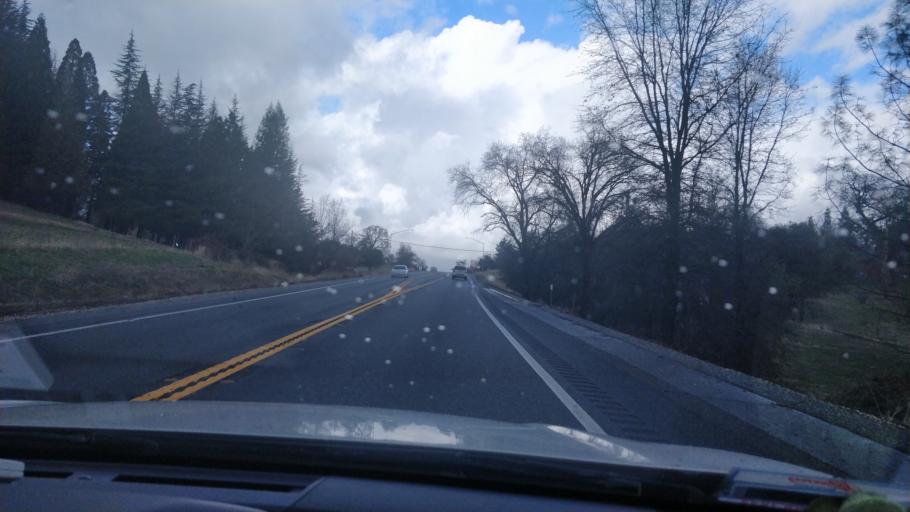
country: US
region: California
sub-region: Nevada County
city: Lake of the Pines
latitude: 39.0652
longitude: -121.0880
